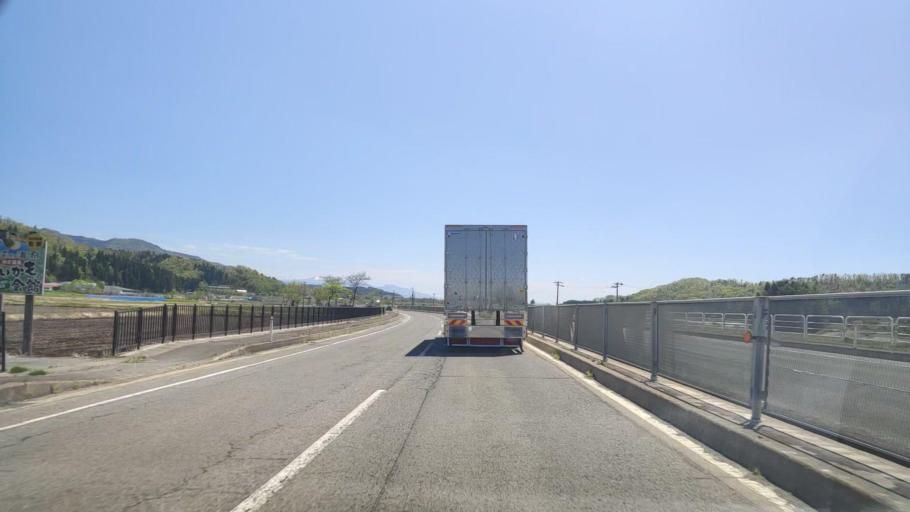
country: JP
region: Yamagata
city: Obanazawa
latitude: 38.5333
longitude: 140.3930
